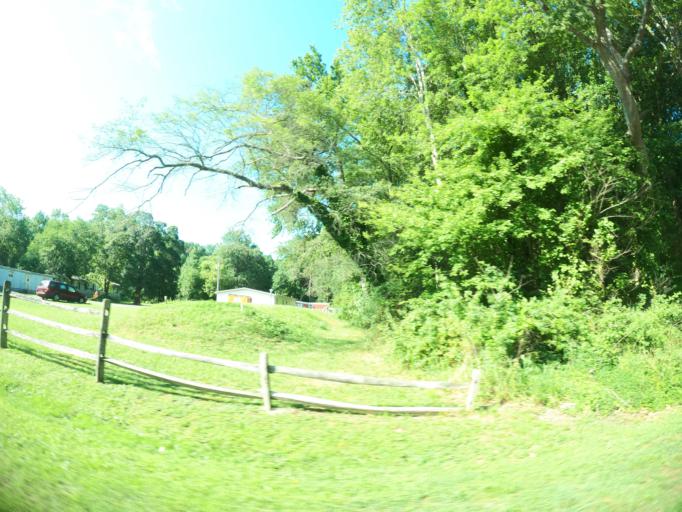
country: US
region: Delaware
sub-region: Sussex County
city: Ocean View
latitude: 38.4928
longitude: -75.1280
